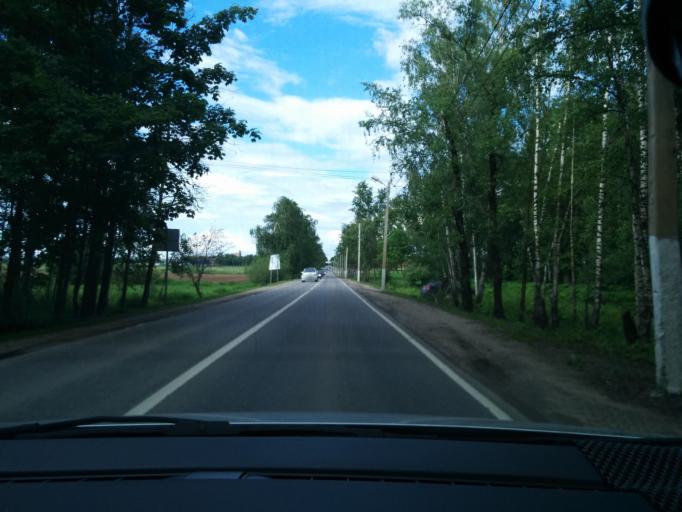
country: RU
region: Moskovskaya
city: Lugovaya
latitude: 56.0376
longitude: 37.4721
